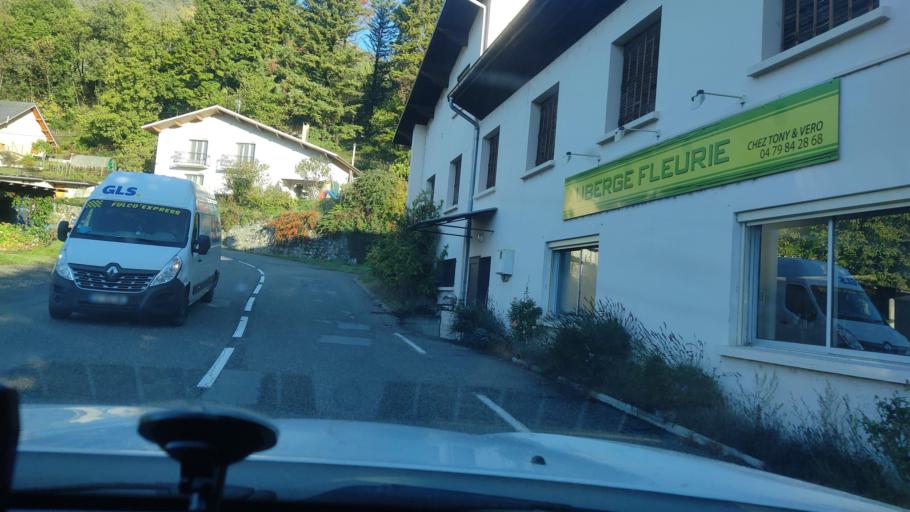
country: FR
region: Rhone-Alpes
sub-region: Departement de la Savoie
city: Cruet
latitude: 45.5177
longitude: 6.0883
